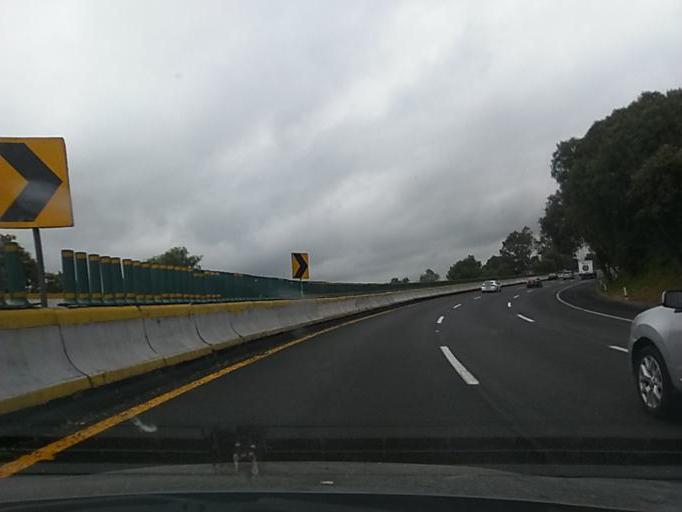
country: MX
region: Mexico City
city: Xochimilco
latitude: 19.2283
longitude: -99.1316
